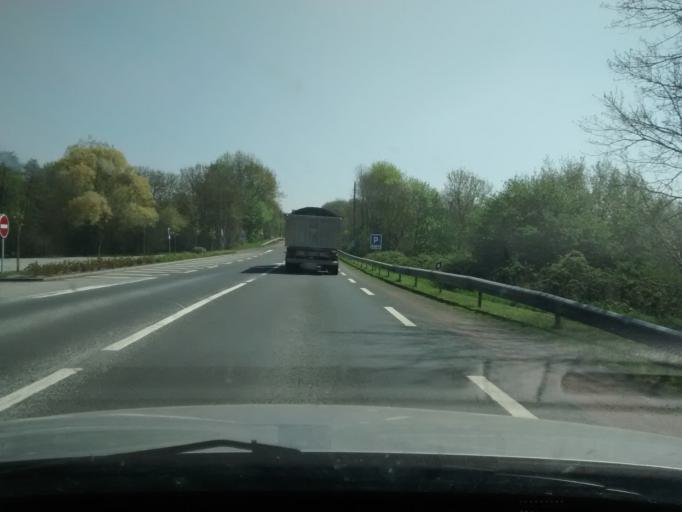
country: FR
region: Pays de la Loire
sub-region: Departement de la Sarthe
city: Loue
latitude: 48.0206
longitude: -0.1139
